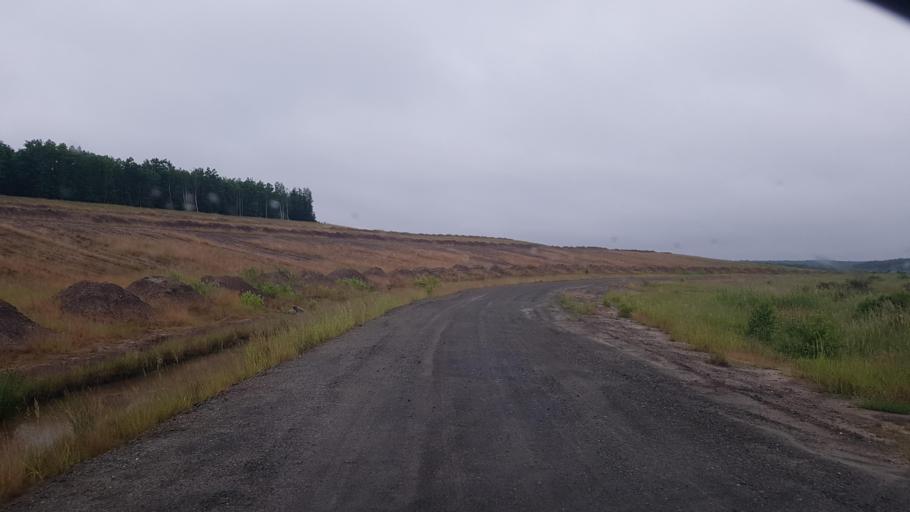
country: DE
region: Brandenburg
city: Lauchhammer
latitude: 51.5347
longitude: 13.7412
